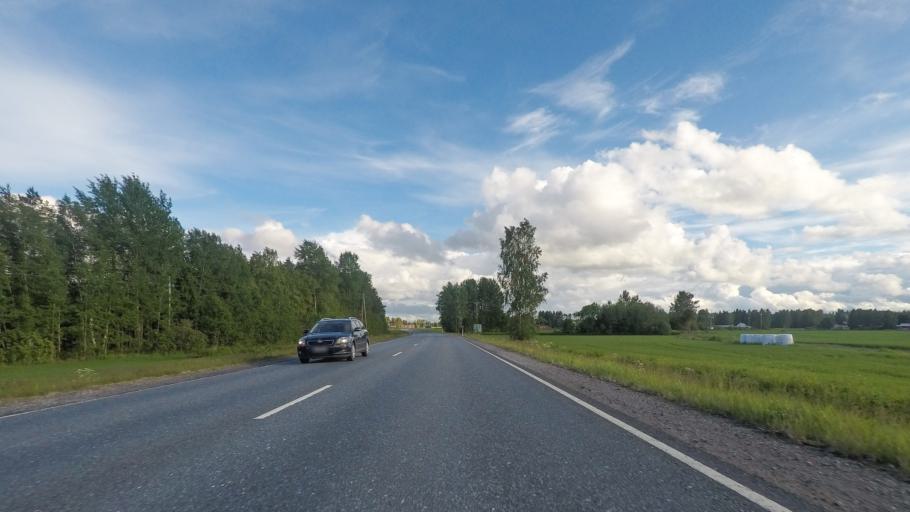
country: FI
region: Paijanne Tavastia
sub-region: Lahti
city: Hartola
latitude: 61.6113
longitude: 26.0072
